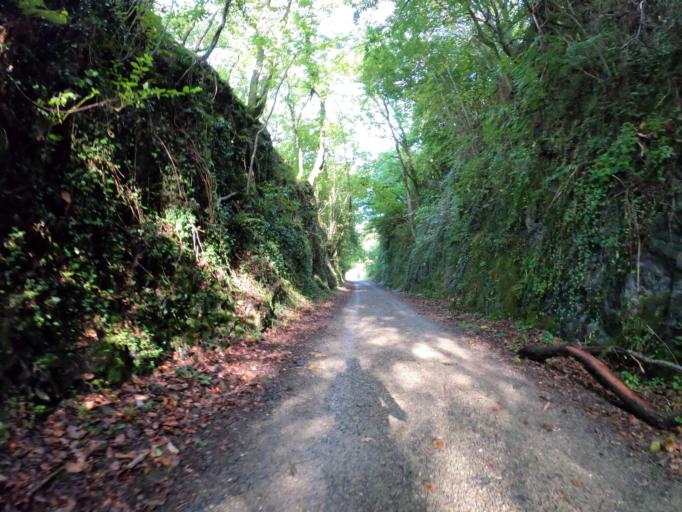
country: ES
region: Navarre
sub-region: Provincia de Navarra
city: Leitza
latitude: 43.0644
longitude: -1.9092
